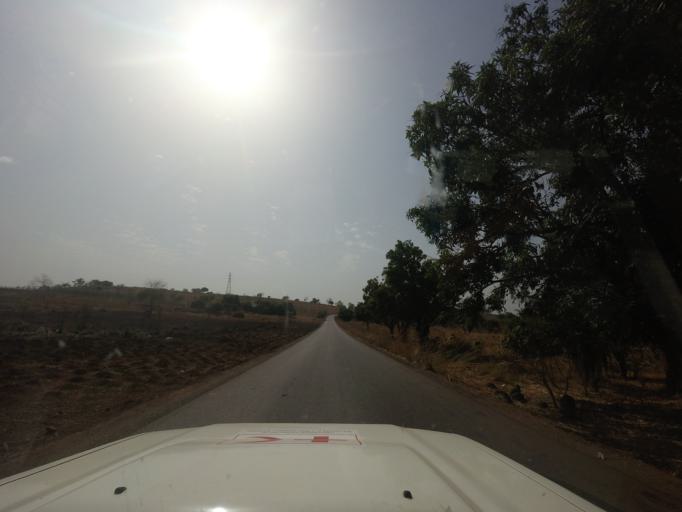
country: GN
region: Mamou
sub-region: Mamou Prefecture
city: Mamou
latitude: 10.1963
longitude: -12.4632
